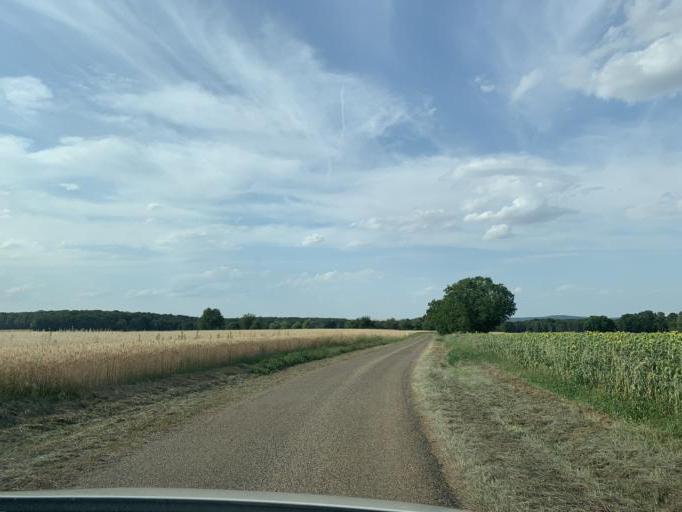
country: FR
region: Bourgogne
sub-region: Departement de l'Yonne
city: Fontenailles
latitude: 47.4995
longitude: 3.4289
